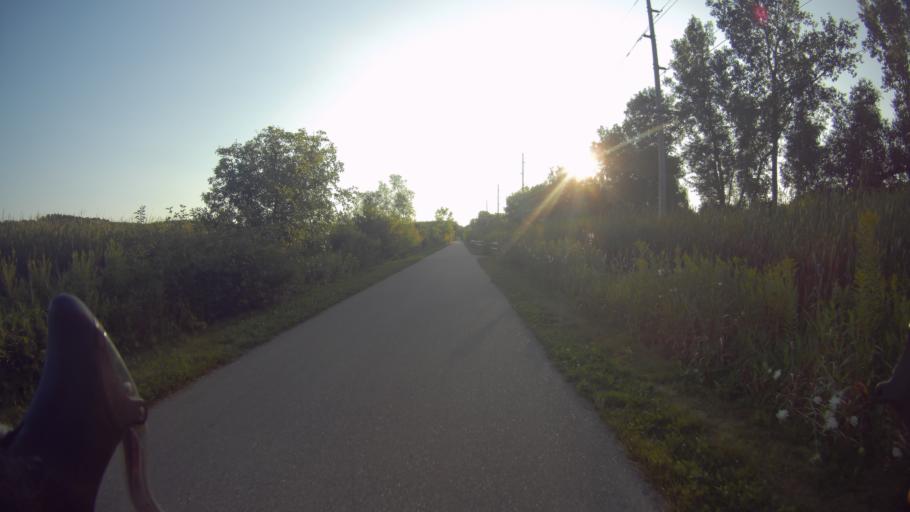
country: US
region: Wisconsin
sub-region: Dane County
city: Shorewood Hills
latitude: 43.0250
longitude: -89.4517
